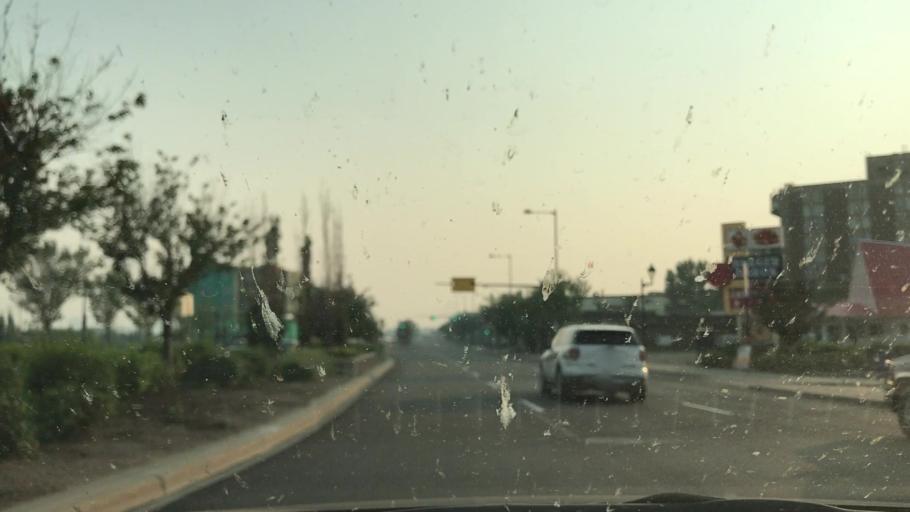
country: CA
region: Alberta
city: Edmonton
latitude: 53.5881
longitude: -113.4364
